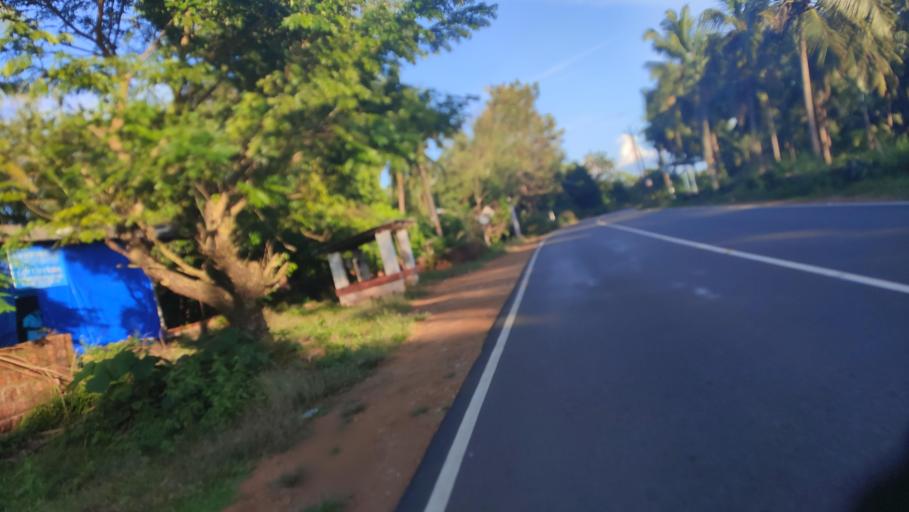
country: IN
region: Kerala
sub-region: Kasaragod District
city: Kasaragod
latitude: 12.4671
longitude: 75.0818
